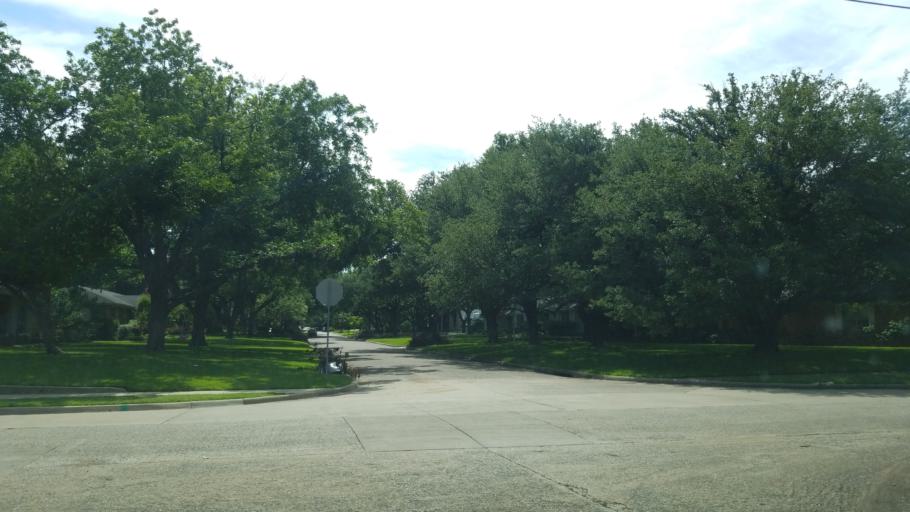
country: US
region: Texas
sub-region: Dallas County
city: Farmers Branch
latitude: 32.9051
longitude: -96.8436
